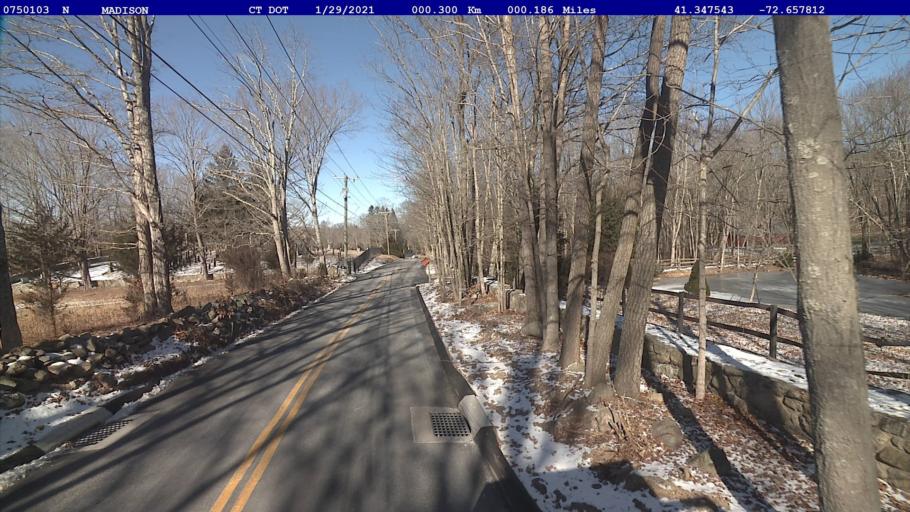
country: US
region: Connecticut
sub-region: New Haven County
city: Guilford
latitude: 41.3476
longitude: -72.6578
